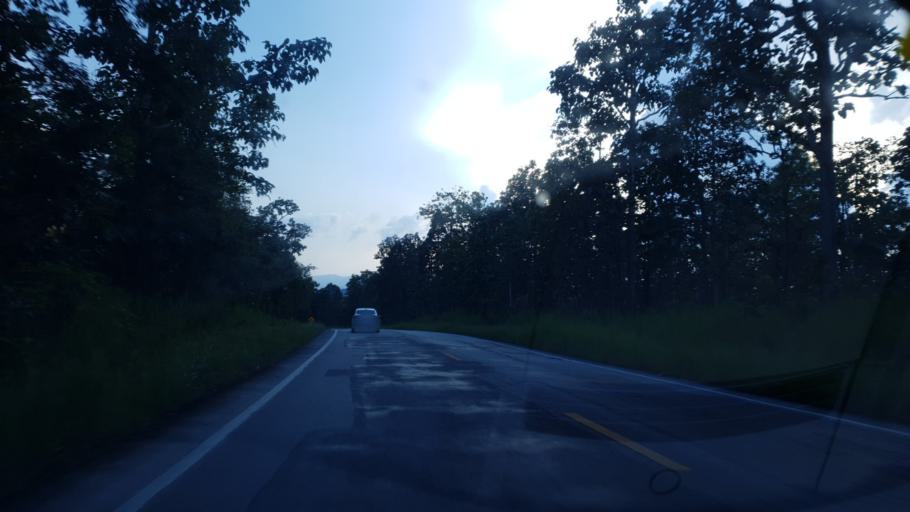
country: TH
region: Mae Hong Son
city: Khun Yuam
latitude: 18.7652
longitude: 97.9347
